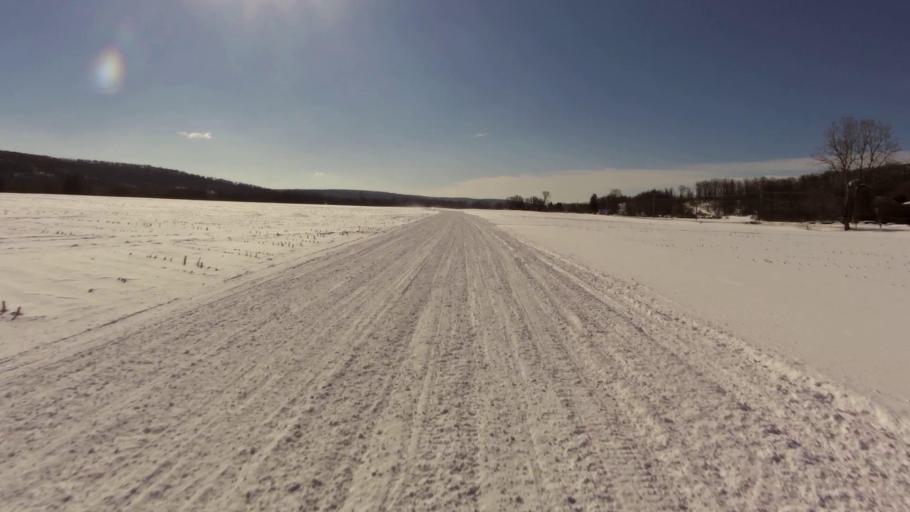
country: US
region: New York
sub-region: Cattaraugus County
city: Franklinville
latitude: 42.3883
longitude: -78.4766
